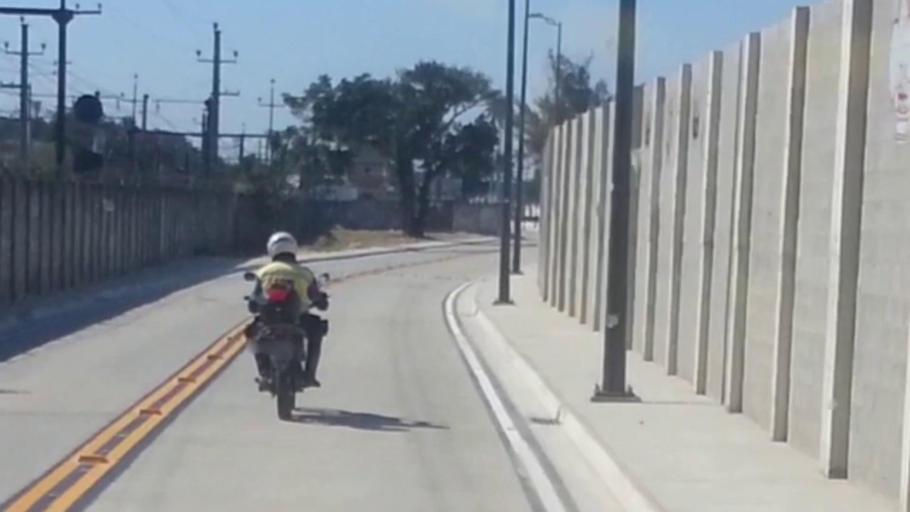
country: BR
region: Rio de Janeiro
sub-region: Nilopolis
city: Nilopolis
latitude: -22.8672
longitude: -43.4112
